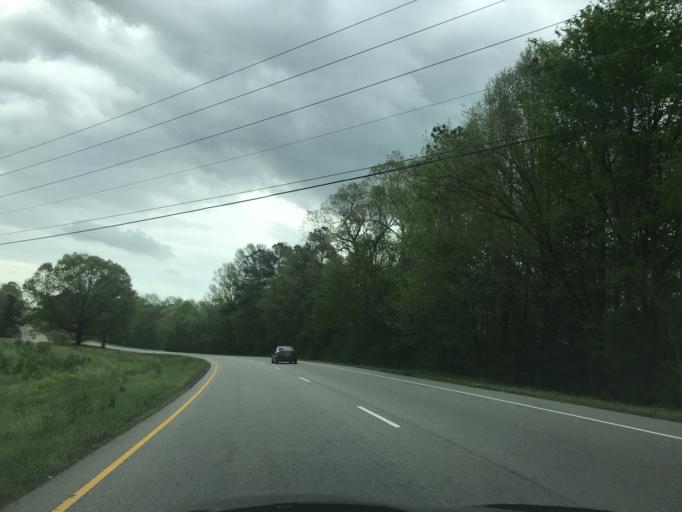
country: US
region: North Carolina
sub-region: Wake County
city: Knightdale
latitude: 35.8041
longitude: -78.4456
